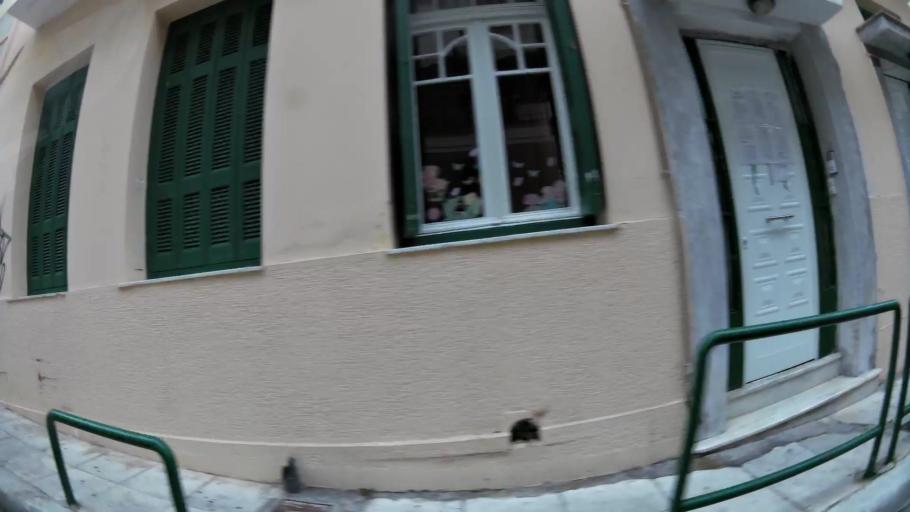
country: GR
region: Attica
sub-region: Nomos Attikis
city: Piraeus
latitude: 37.9293
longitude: 23.6419
